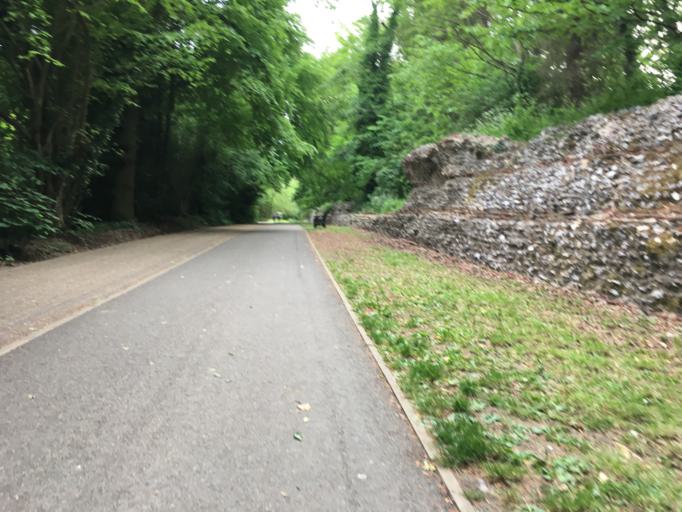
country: GB
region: England
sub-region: Hertfordshire
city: St Albans
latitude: 51.7469
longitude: -0.3537
